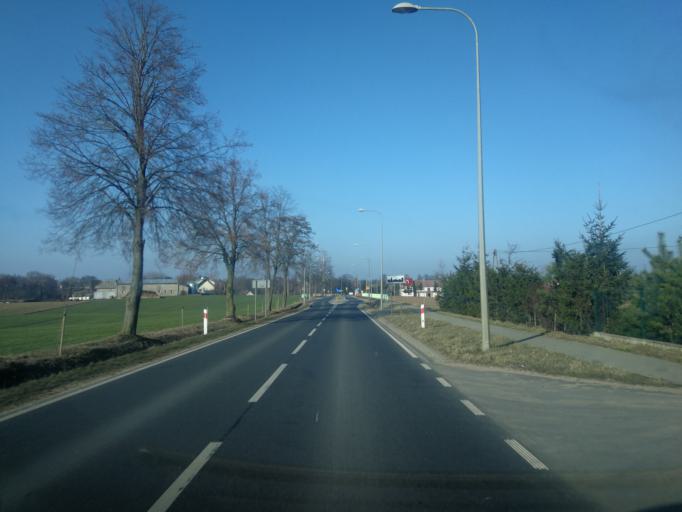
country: PL
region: Warmian-Masurian Voivodeship
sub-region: Powiat ilawski
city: Lubawa
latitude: 53.4523
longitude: 19.7782
